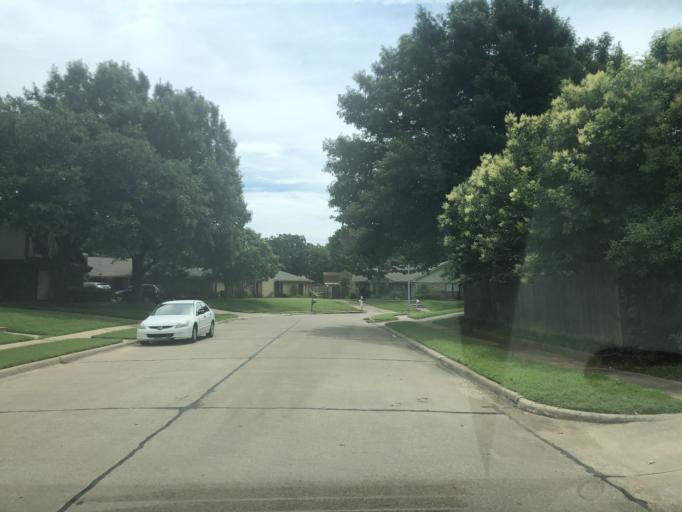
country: US
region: Texas
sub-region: Dallas County
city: Irving
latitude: 32.7988
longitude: -96.9824
